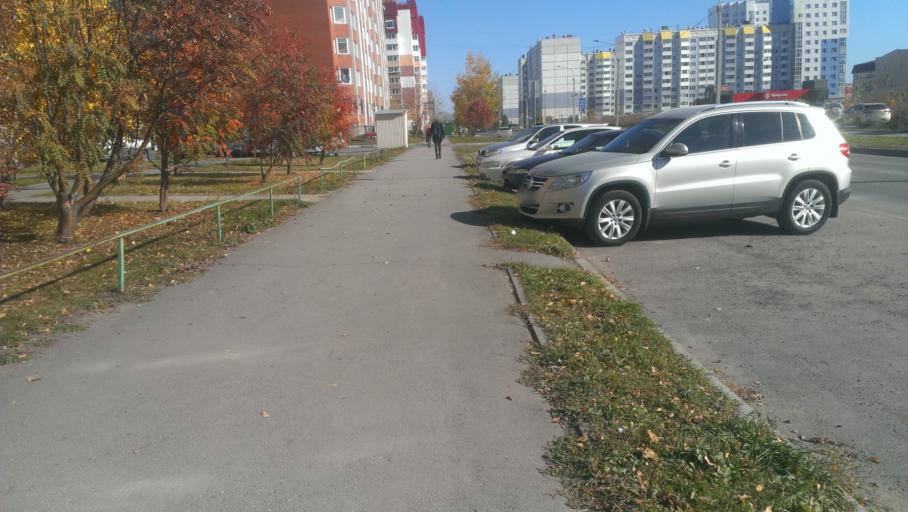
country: RU
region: Altai Krai
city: Novosilikatnyy
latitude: 53.3302
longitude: 83.6816
